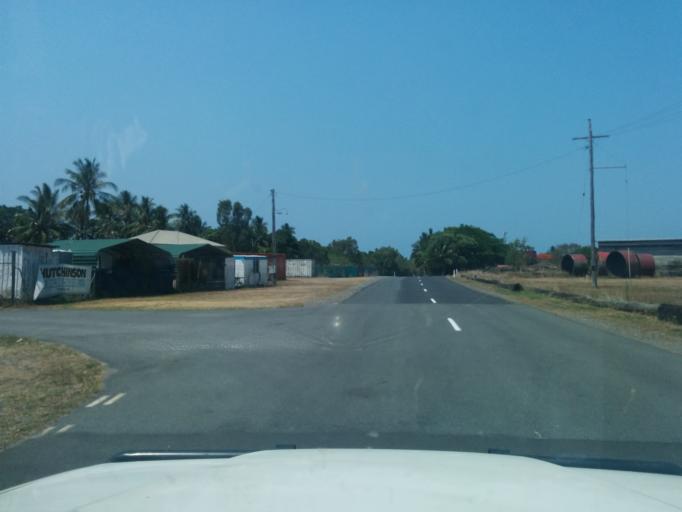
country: AU
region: Queensland
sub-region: Cairns
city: Redlynch
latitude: -16.8738
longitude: 145.7347
